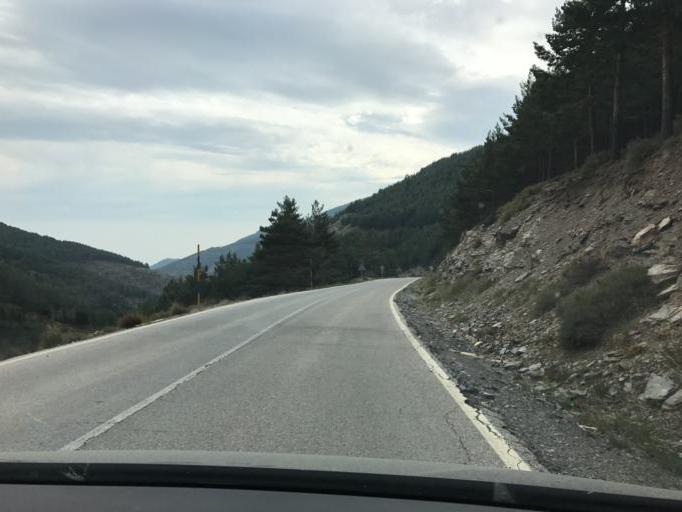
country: ES
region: Andalusia
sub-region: Provincia de Almeria
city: Bayarcal
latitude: 37.0988
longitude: -3.0227
